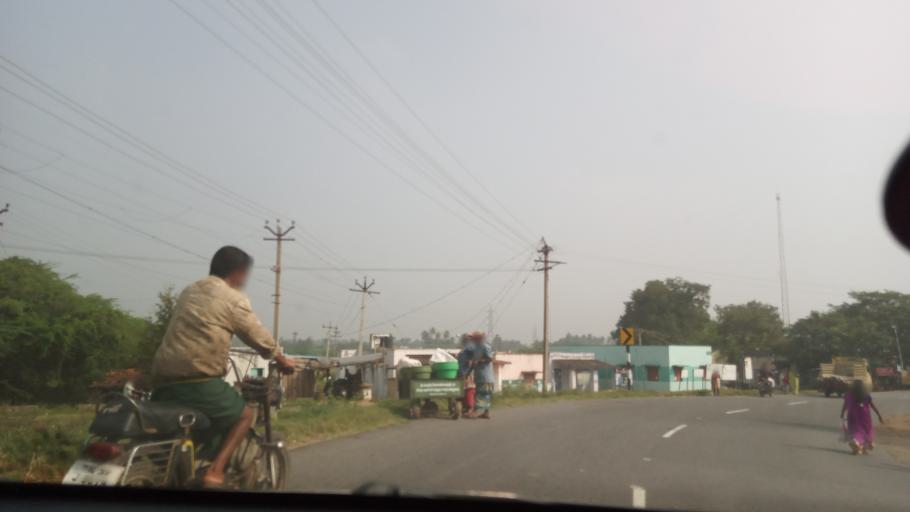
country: IN
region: Tamil Nadu
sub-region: Erode
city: Punjai Puliyampatti
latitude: 11.4032
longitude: 77.1900
